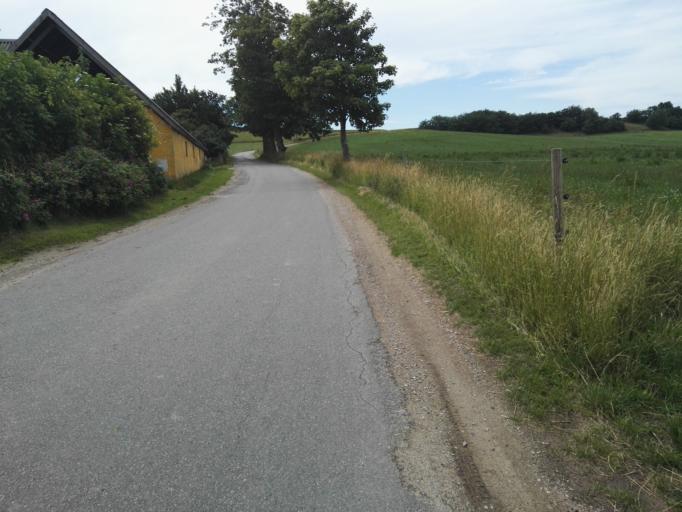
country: DK
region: Capital Region
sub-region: Hillerod Kommune
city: Skaevinge
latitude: 55.8917
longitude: 12.1387
